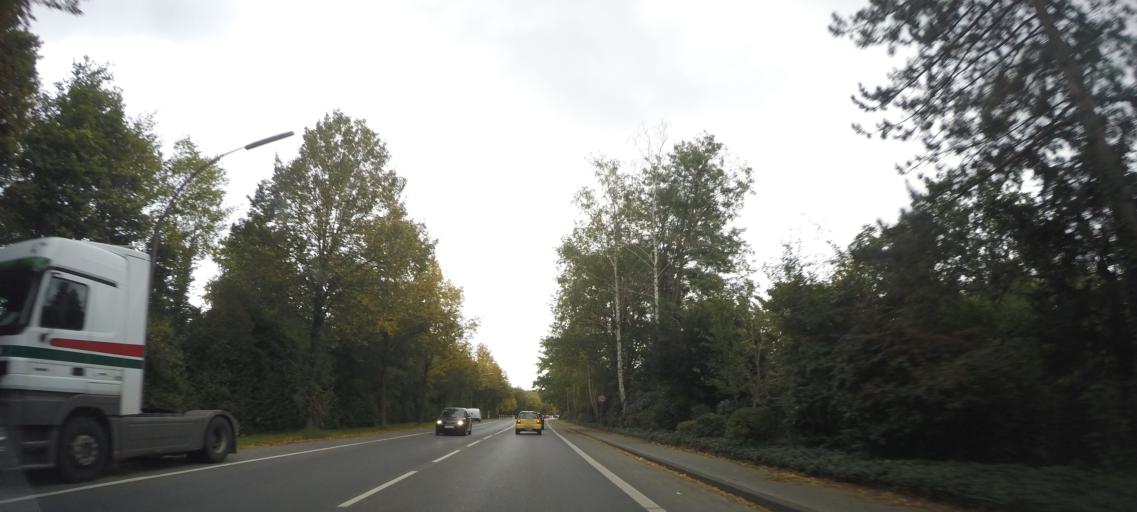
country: DE
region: North Rhine-Westphalia
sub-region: Regierungsbezirk Arnsberg
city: Lippstadt
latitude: 51.6830
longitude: 8.3579
